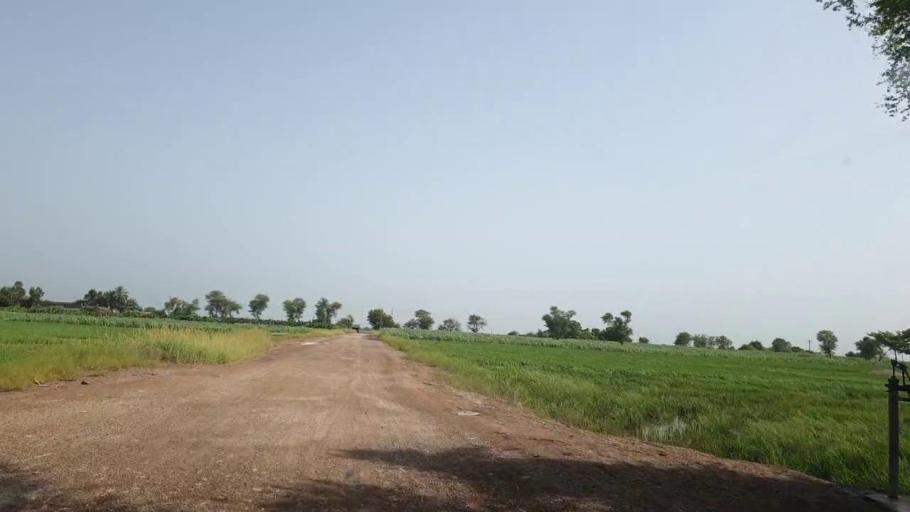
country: PK
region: Sindh
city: Sakrand
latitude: 26.2941
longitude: 68.2214
